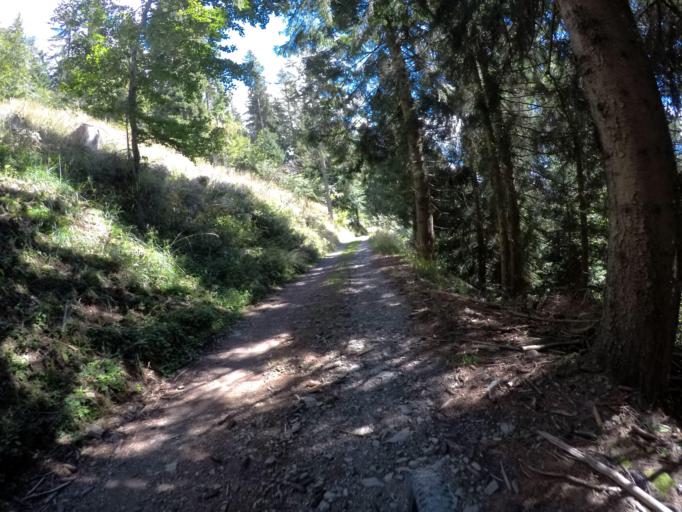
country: IT
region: Friuli Venezia Giulia
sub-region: Provincia di Udine
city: Paularo
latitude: 46.5507
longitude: 13.1314
